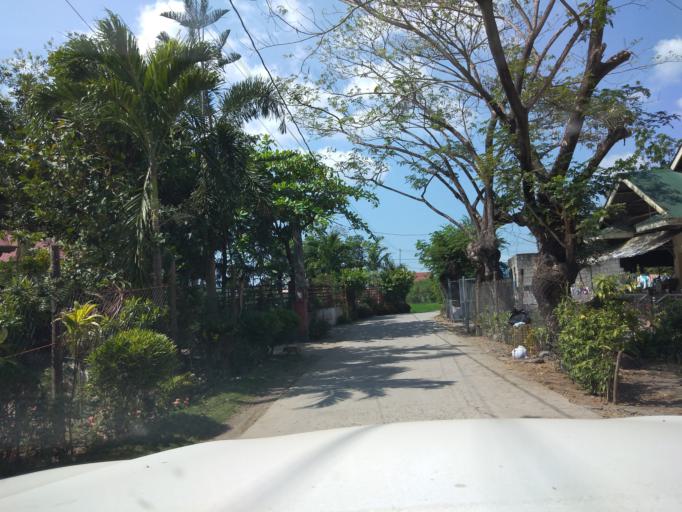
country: PH
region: Central Luzon
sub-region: Province of Pampanga
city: Bahay Pare
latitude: 15.0468
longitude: 120.8834
